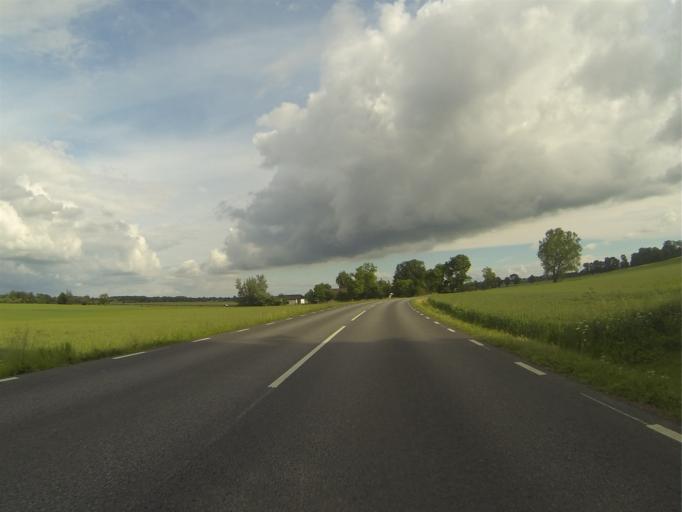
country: SE
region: Skane
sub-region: Eslovs Kommun
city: Eslov
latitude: 55.7549
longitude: 13.3210
